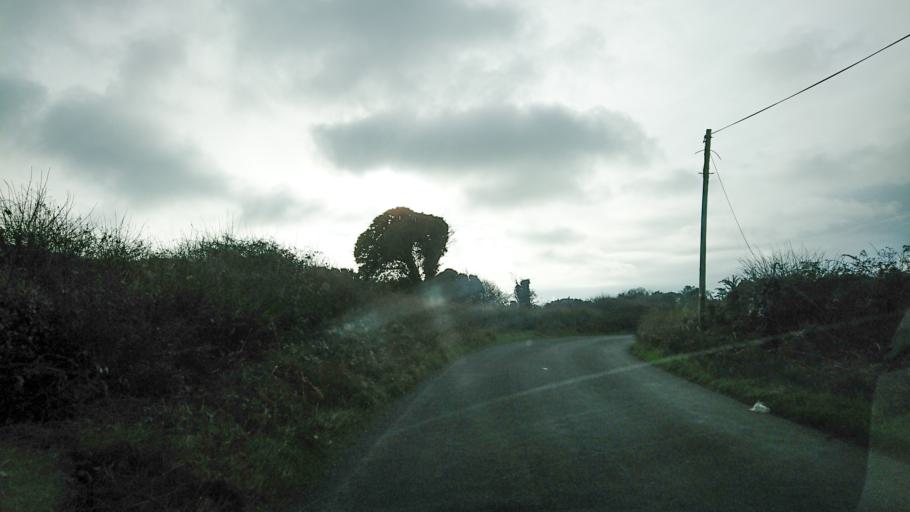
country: IE
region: Munster
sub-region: Waterford
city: Tra Mhor
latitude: 52.1800
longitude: -7.1734
